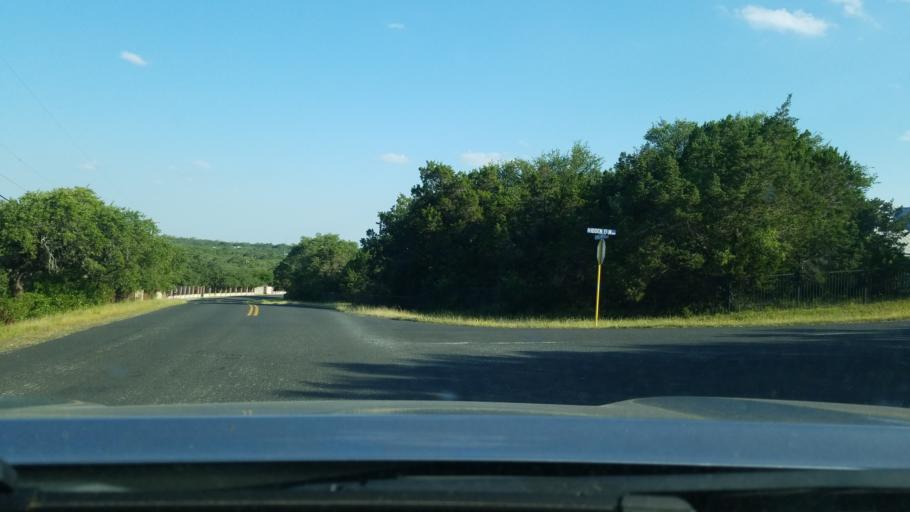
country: US
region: Texas
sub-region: Bexar County
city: Timberwood Park
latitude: 29.7010
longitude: -98.4373
